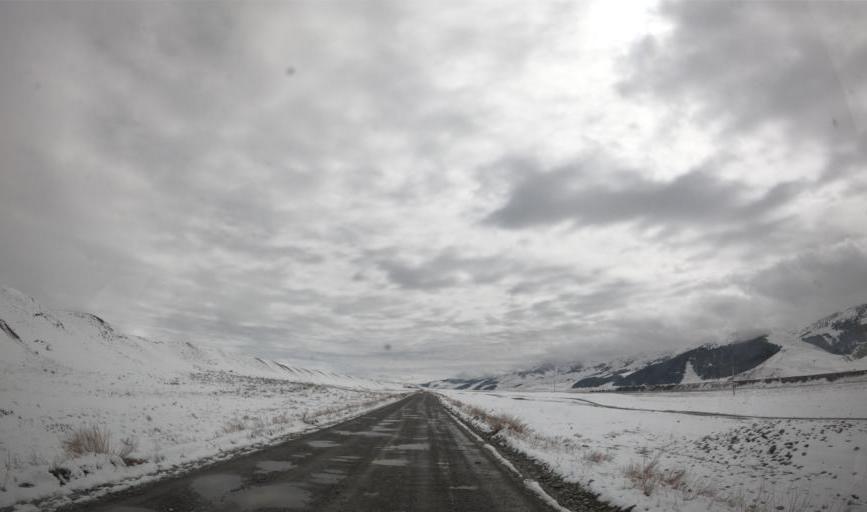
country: KG
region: Naryn
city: Naryn
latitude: 41.2360
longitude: 76.2518
